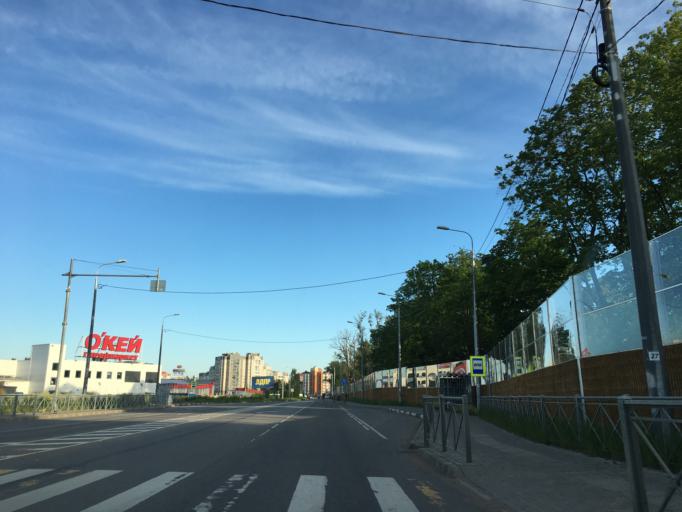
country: RU
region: Leningrad
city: Gatchina
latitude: 59.5849
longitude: 30.1364
